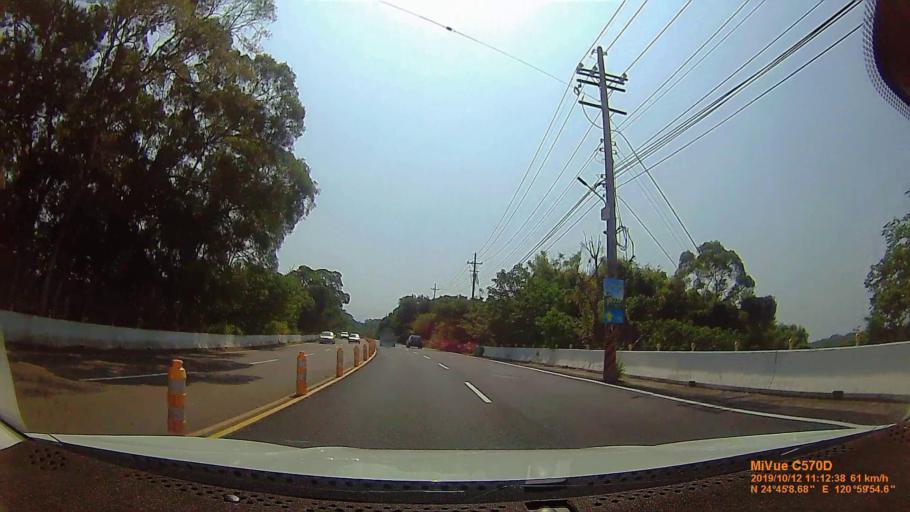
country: TW
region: Taiwan
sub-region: Hsinchu
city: Hsinchu
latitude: 24.7523
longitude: 120.9985
